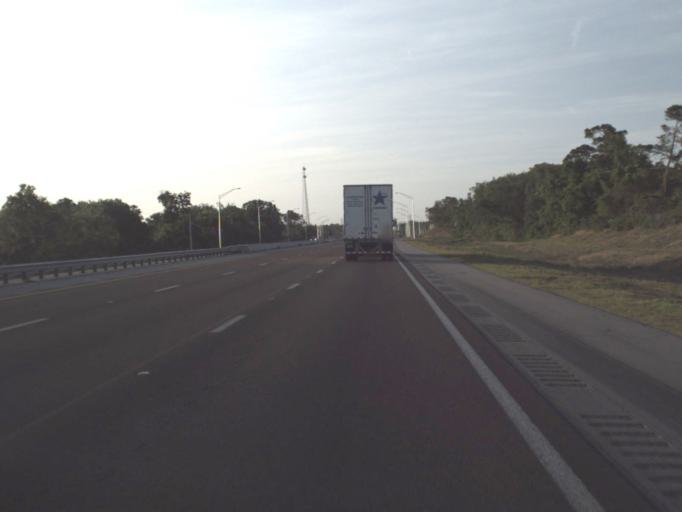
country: US
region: Florida
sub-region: Brevard County
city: Mims
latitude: 28.6568
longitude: -80.8657
